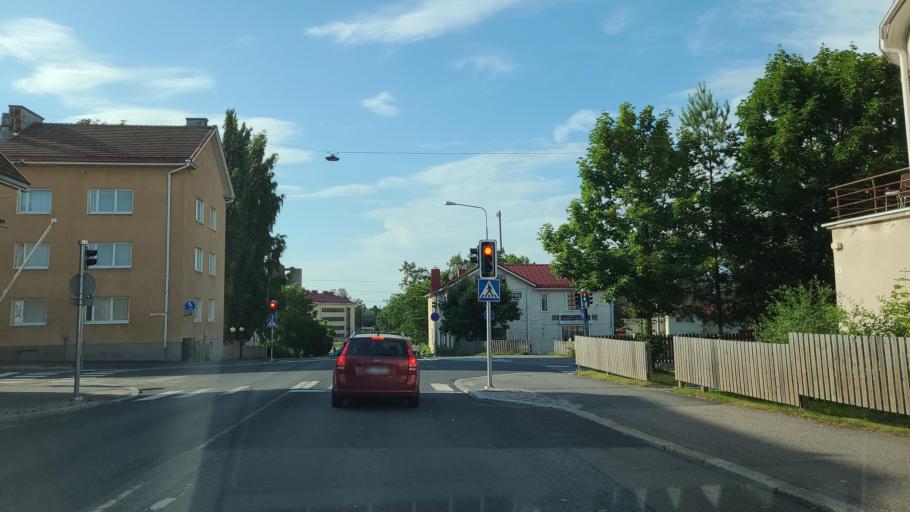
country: FI
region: Ostrobothnia
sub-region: Vaasa
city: Vaasa
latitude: 63.1035
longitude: 21.6189
